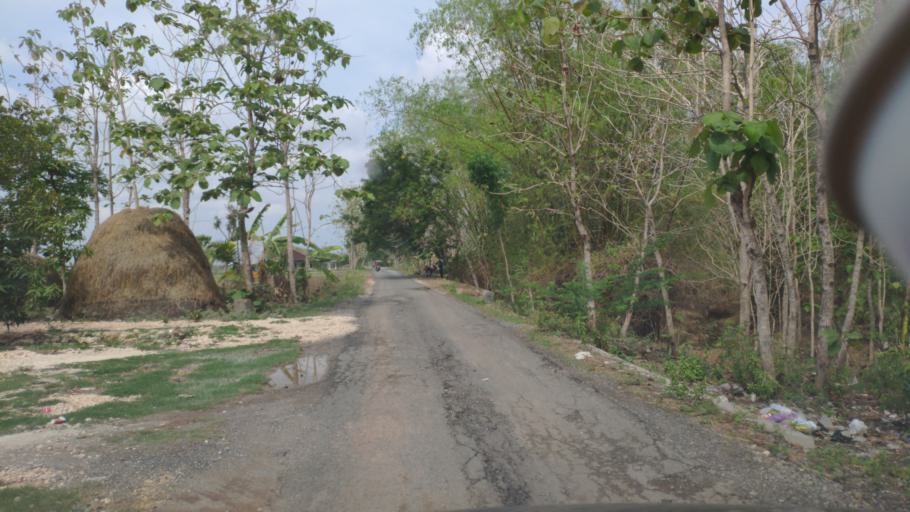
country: ID
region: Central Java
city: Klopoduwur
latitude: -7.0192
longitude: 111.4002
